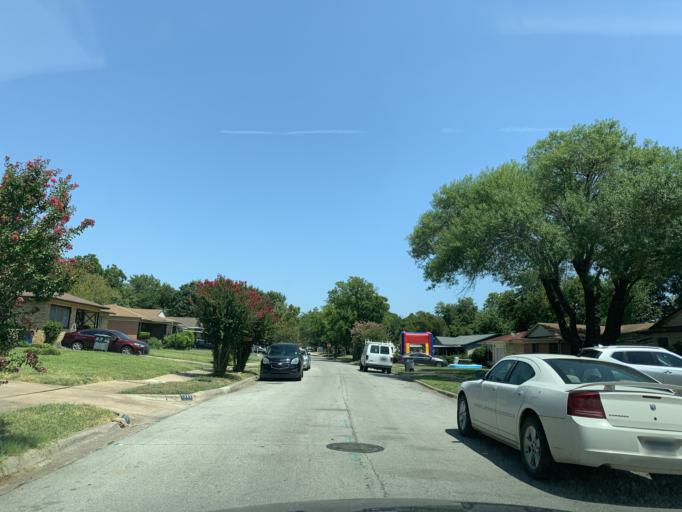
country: US
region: Texas
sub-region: Dallas County
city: Hutchins
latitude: 32.6853
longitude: -96.8032
